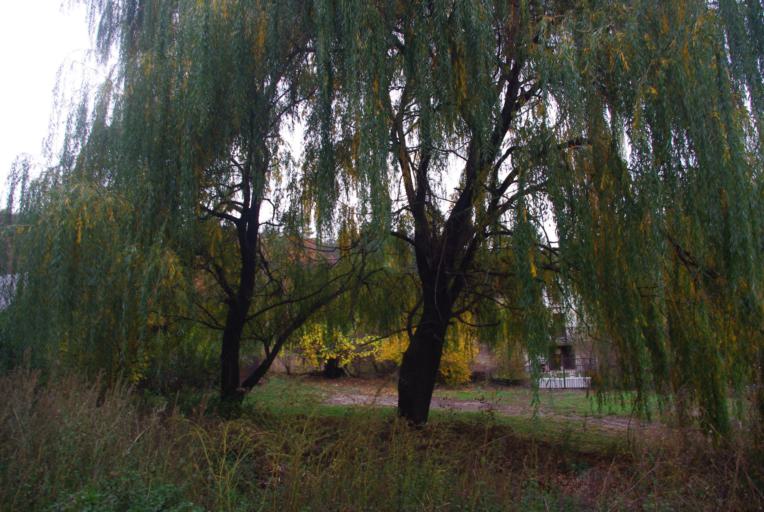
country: HU
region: Borsod-Abauj-Zemplen
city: Satoraljaujhely
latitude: 48.3903
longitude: 21.6364
